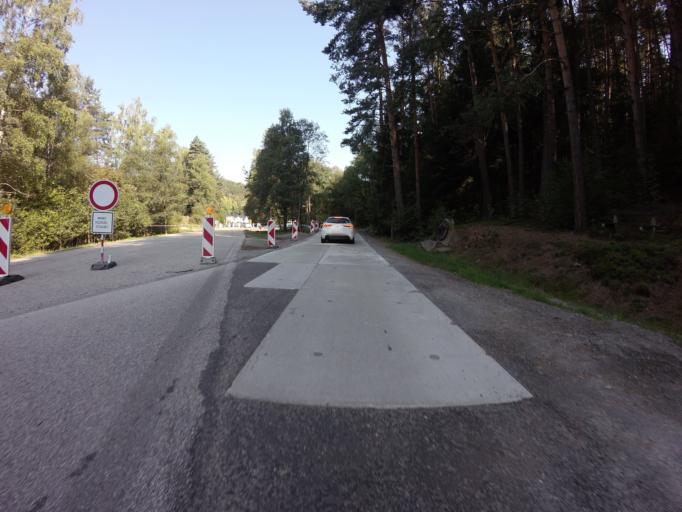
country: CZ
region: Jihocesky
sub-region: Okres Cesky Krumlov
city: Vyssi Brod
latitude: 48.5757
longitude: 14.3205
